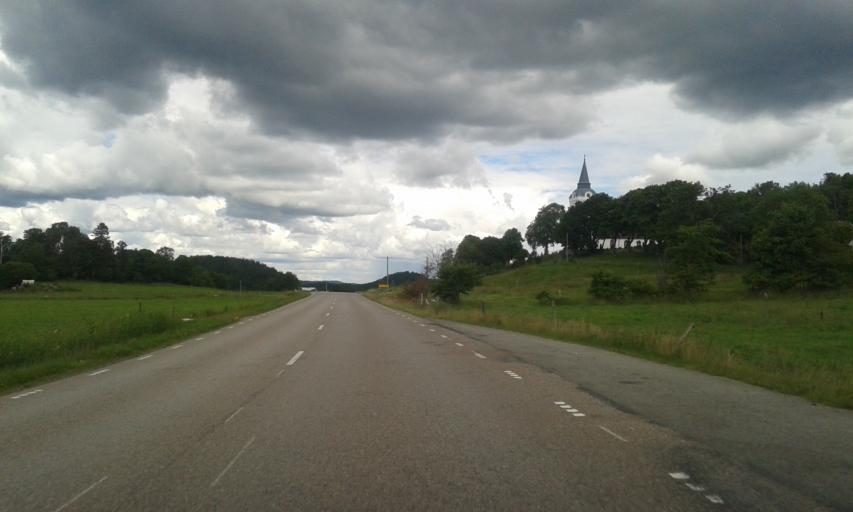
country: SE
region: Vaestra Goetaland
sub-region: Lilla Edets Kommun
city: Lilla Edet
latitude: 58.0880
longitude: 12.1186
